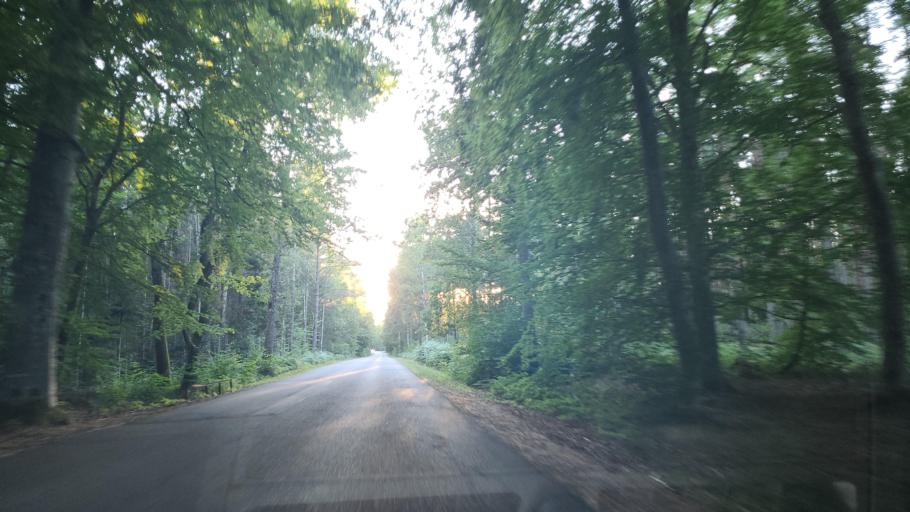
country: SE
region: Kalmar
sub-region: Borgholms Kommun
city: Borgholm
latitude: 57.2779
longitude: 17.0300
